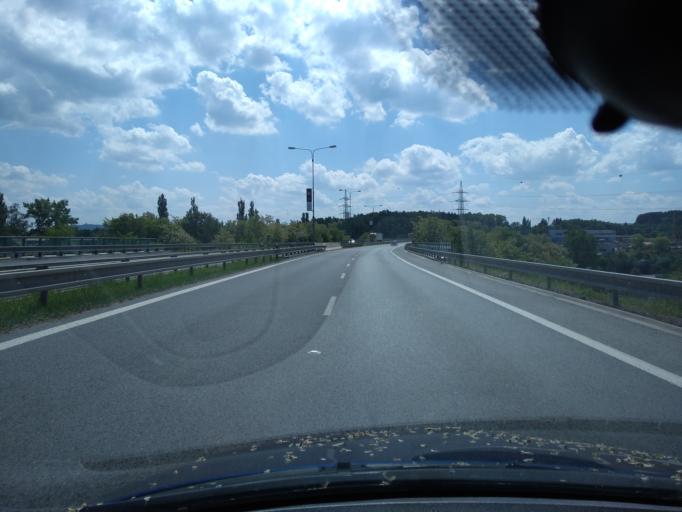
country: CZ
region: Plzensky
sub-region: Okres Plzen-Mesto
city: Pilsen
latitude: 49.7201
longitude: 13.3593
